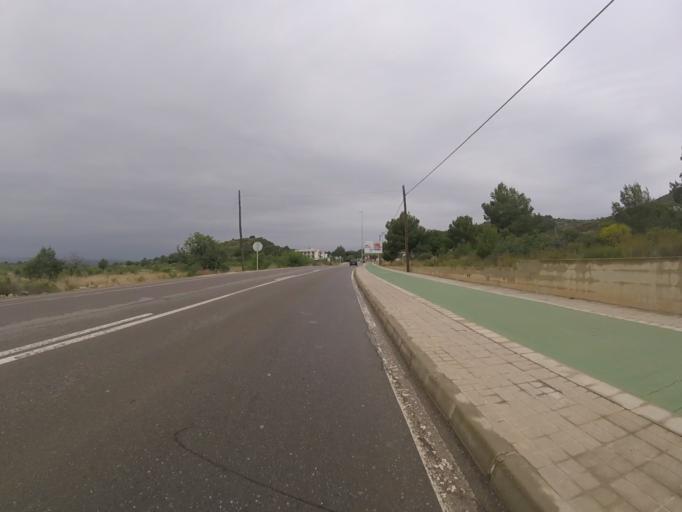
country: ES
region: Valencia
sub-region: Provincia de Castello
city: Alcoceber
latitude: 40.2478
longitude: 0.2557
